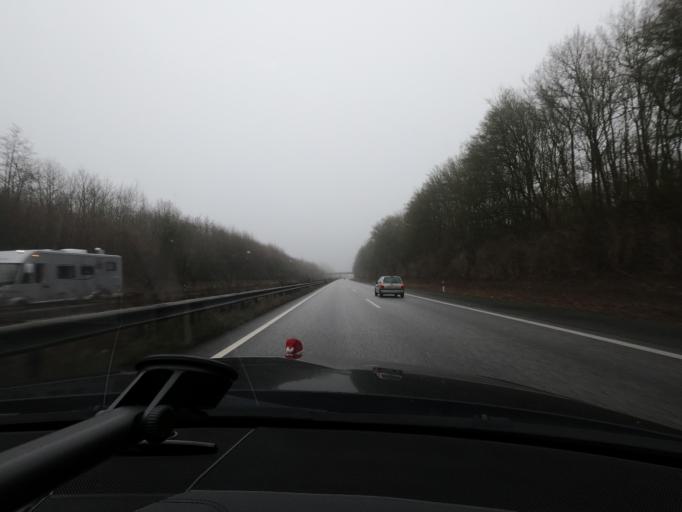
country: DE
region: Schleswig-Holstein
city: Dannewerk
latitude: 54.4973
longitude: 9.5155
